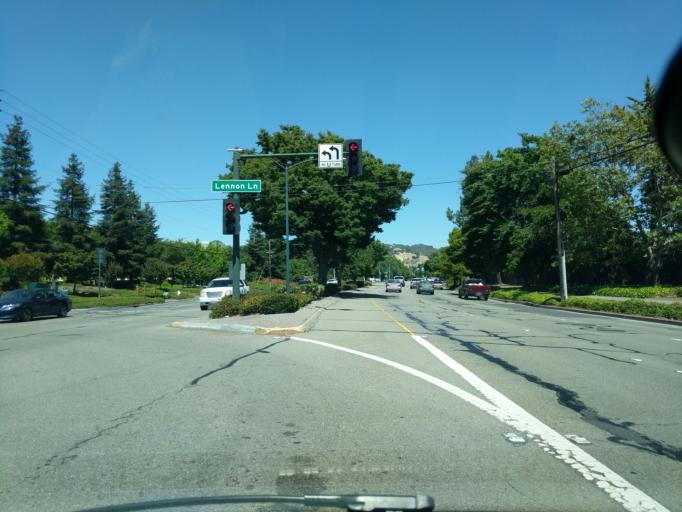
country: US
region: California
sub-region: Contra Costa County
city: Waldon
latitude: 37.9239
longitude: -122.0268
